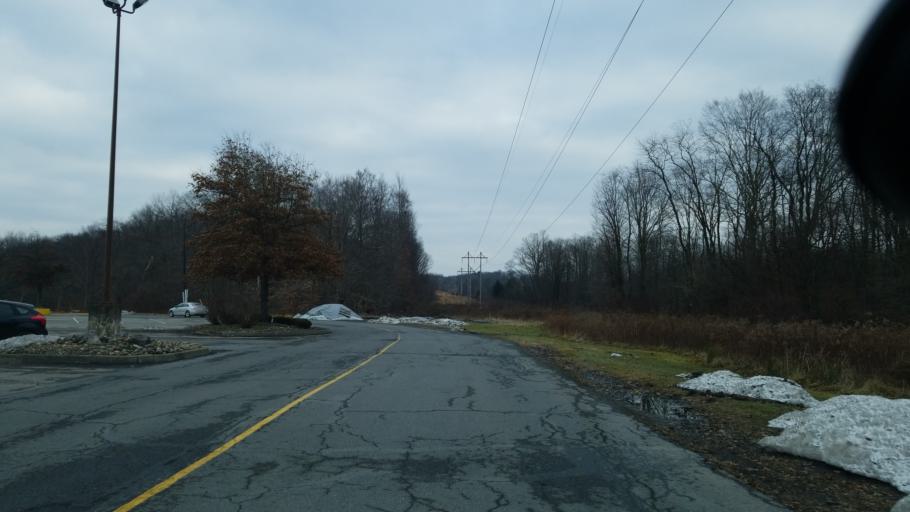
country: US
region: Pennsylvania
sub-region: Clearfield County
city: DuBois
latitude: 41.1188
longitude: -78.7262
